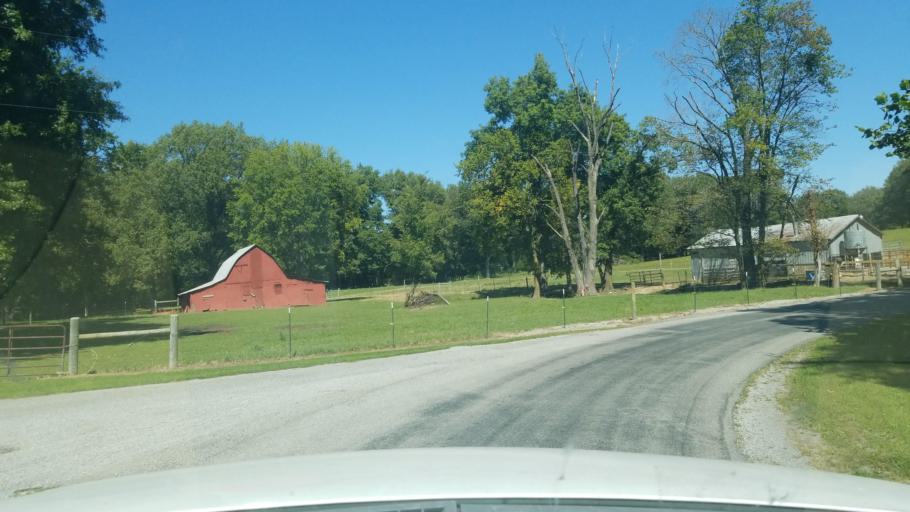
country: US
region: Illinois
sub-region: Saline County
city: Eldorado
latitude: 37.8524
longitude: -88.5165
